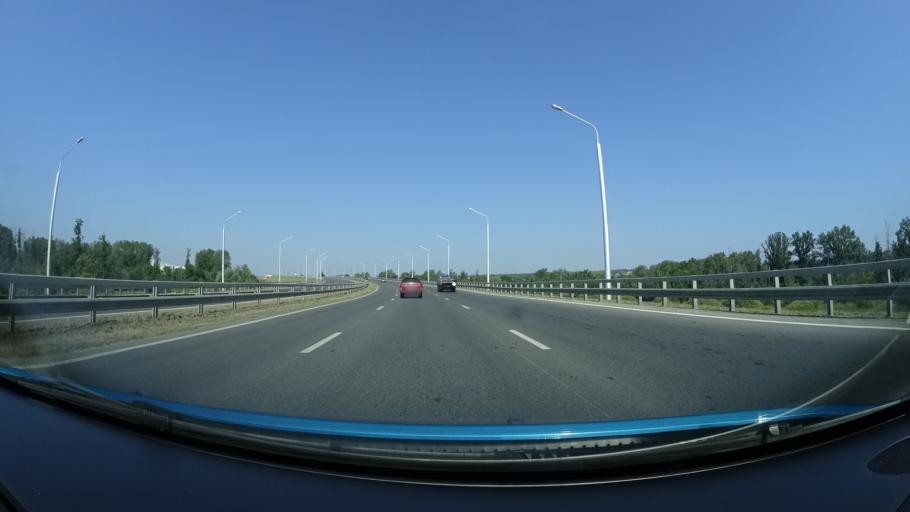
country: RU
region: Bashkortostan
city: Mikhaylovka
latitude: 54.7961
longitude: 55.9001
